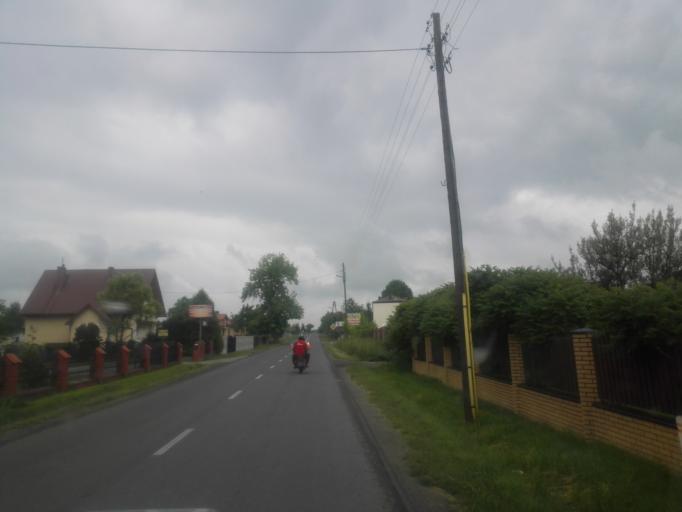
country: PL
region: Silesian Voivodeship
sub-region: Powiat czestochowski
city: Olsztyn
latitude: 50.7401
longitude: 19.3292
